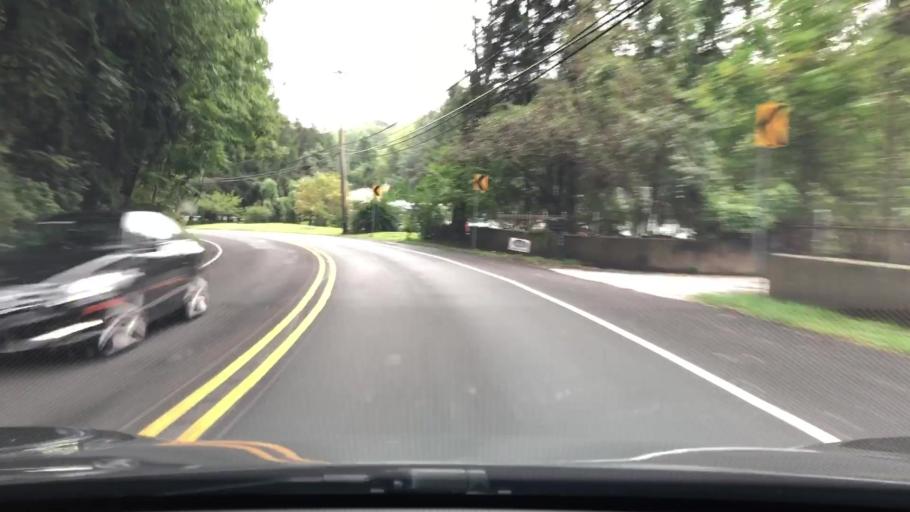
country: US
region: Pennsylvania
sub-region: Delaware County
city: Broomall
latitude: 39.9969
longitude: -75.3581
